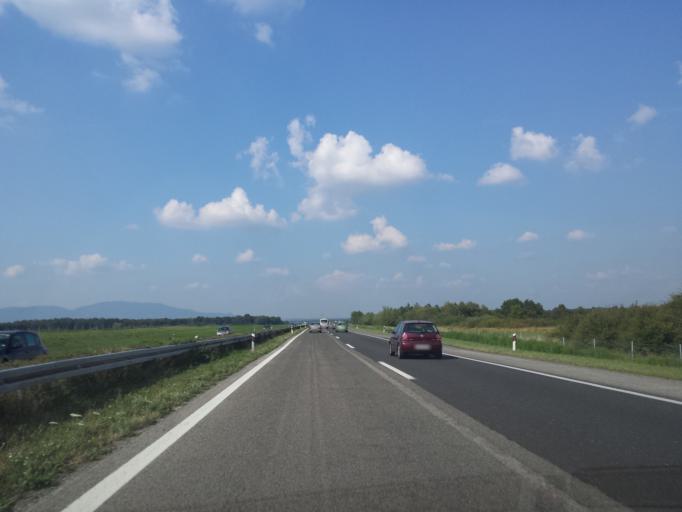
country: HR
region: Zagrebacka
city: Jastrebarsko
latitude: 45.6060
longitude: 15.6382
